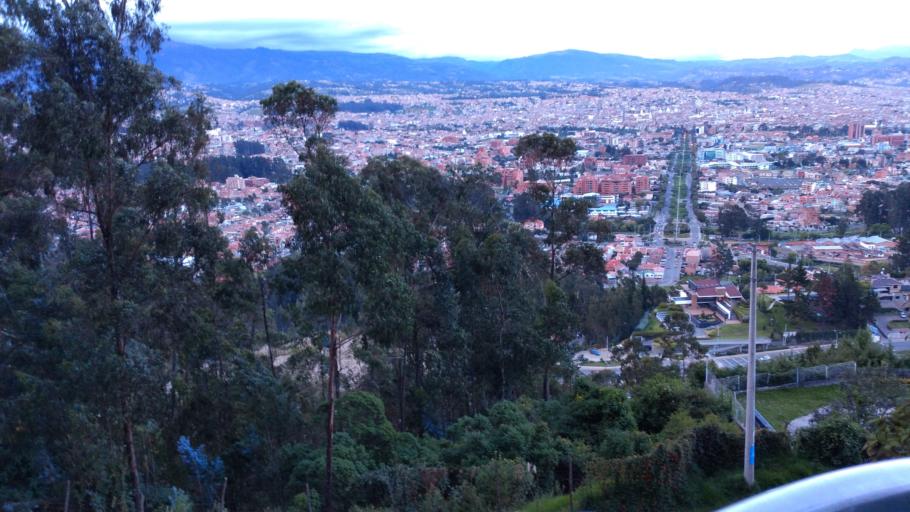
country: EC
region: Azuay
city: Cuenca
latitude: -2.9223
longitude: -79.0115
